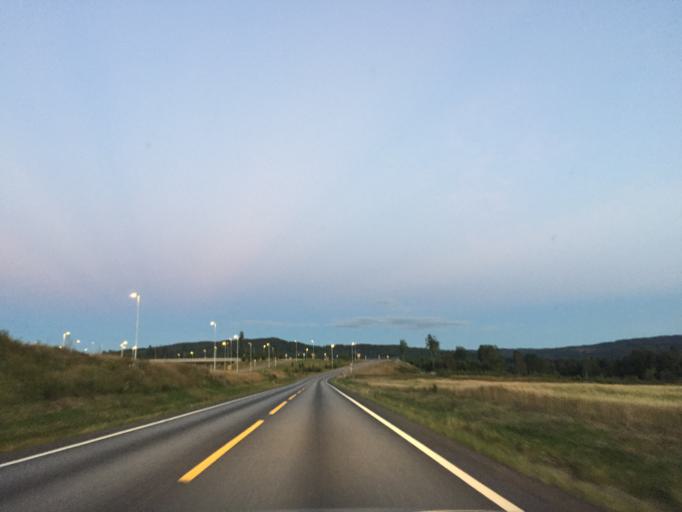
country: NO
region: Hedmark
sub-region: Kongsvinger
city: Spetalen
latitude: 60.2106
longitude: 11.8849
